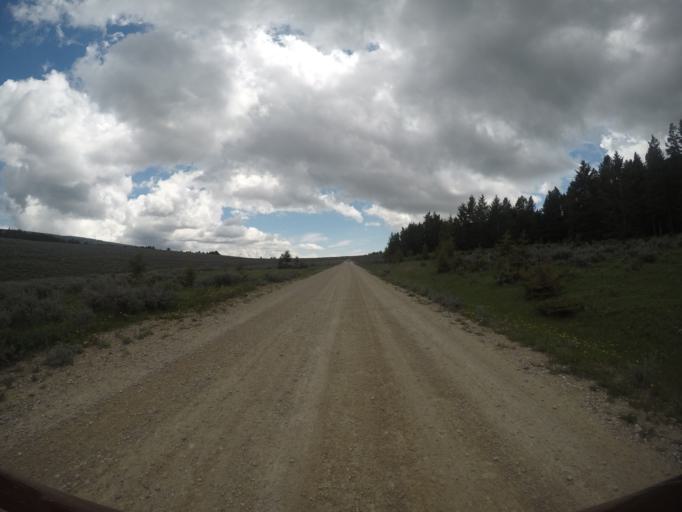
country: US
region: Wyoming
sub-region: Big Horn County
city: Lovell
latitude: 45.1737
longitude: -108.4563
